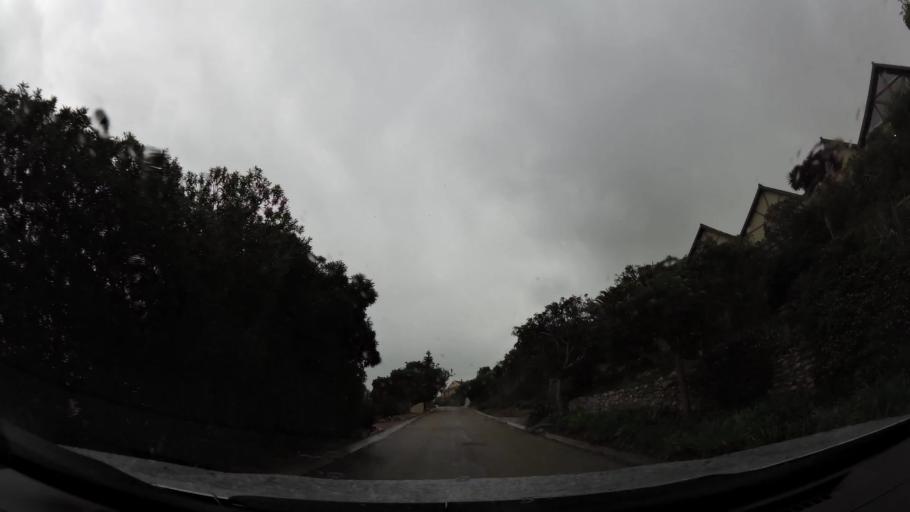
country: ZA
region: Western Cape
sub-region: Eden District Municipality
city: George
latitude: -34.0468
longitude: 22.2882
